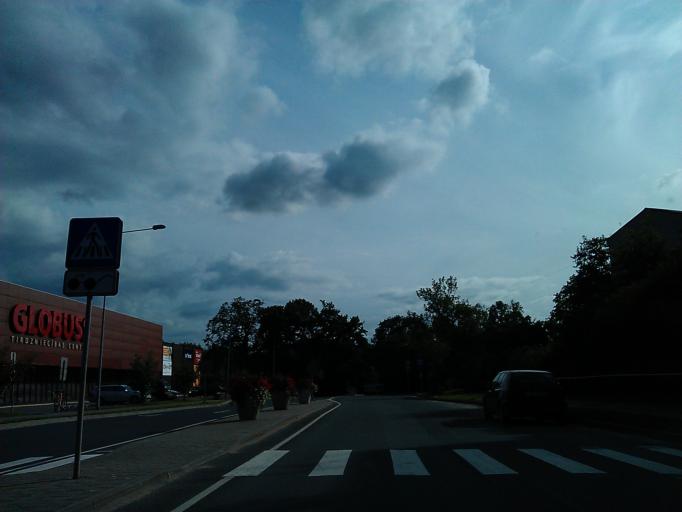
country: LV
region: Cesu Rajons
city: Cesis
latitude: 57.3102
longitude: 25.2774
